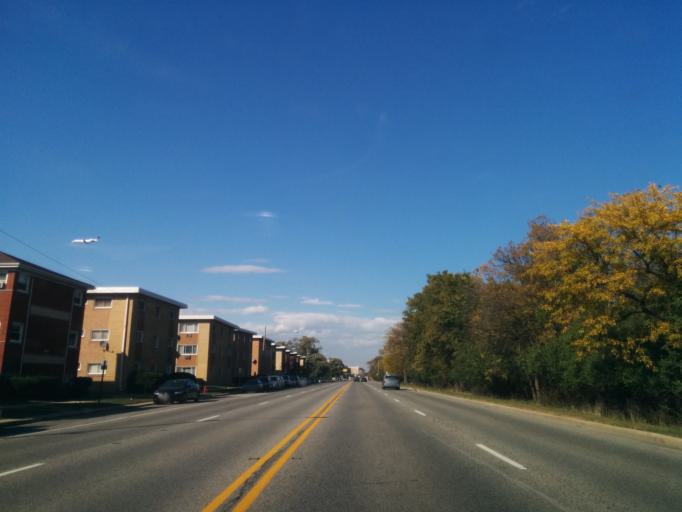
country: US
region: Illinois
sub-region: Cook County
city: Schiller Park
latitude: 41.9606
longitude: -87.8611
